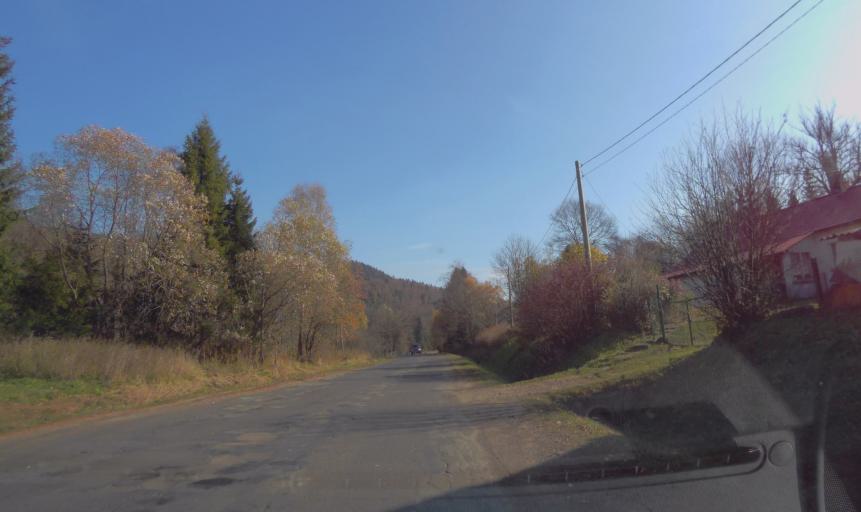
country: PL
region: Subcarpathian Voivodeship
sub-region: Powiat leski
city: Cisna
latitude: 49.2094
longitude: 22.2676
